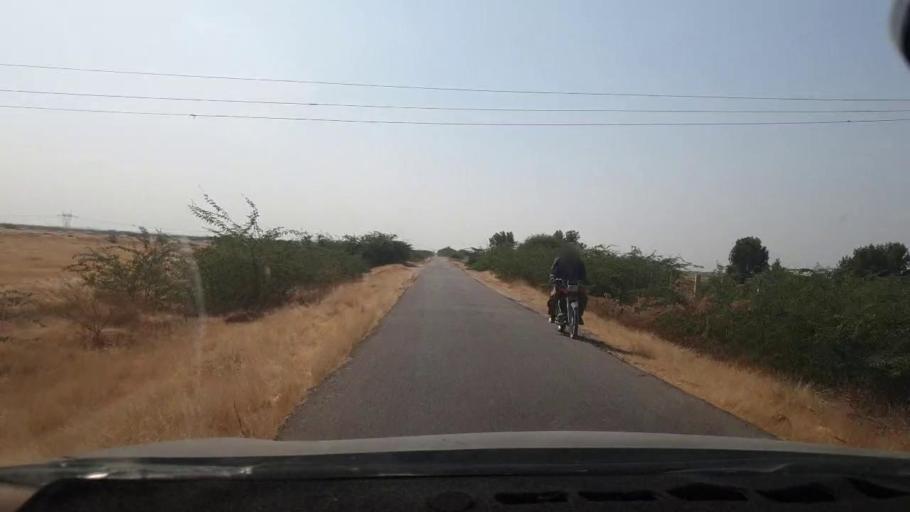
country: PK
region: Sindh
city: Malir Cantonment
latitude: 25.1217
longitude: 67.2182
